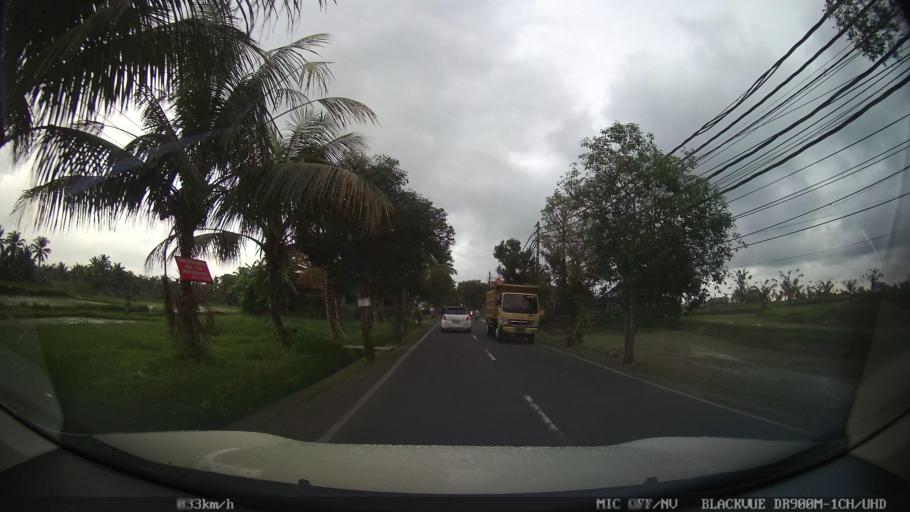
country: ID
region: Bali
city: Bayad
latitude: -8.4522
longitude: 115.2430
